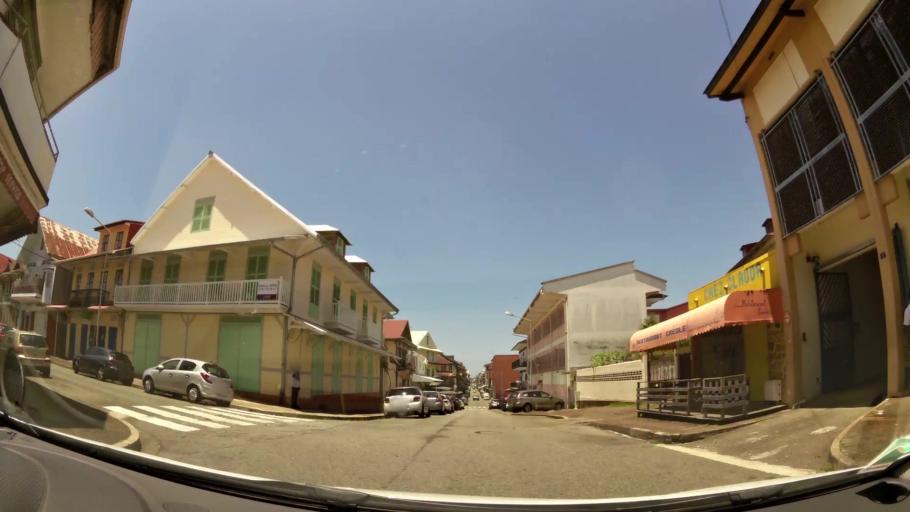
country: GF
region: Guyane
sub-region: Guyane
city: Cayenne
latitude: 4.9374
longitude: -52.3347
